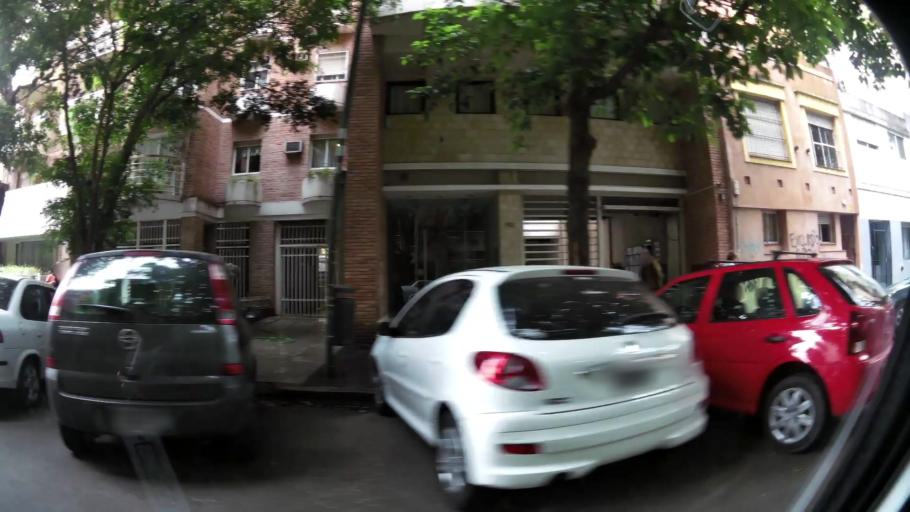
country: AR
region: Buenos Aires F.D.
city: Colegiales
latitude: -34.5549
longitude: -58.4566
